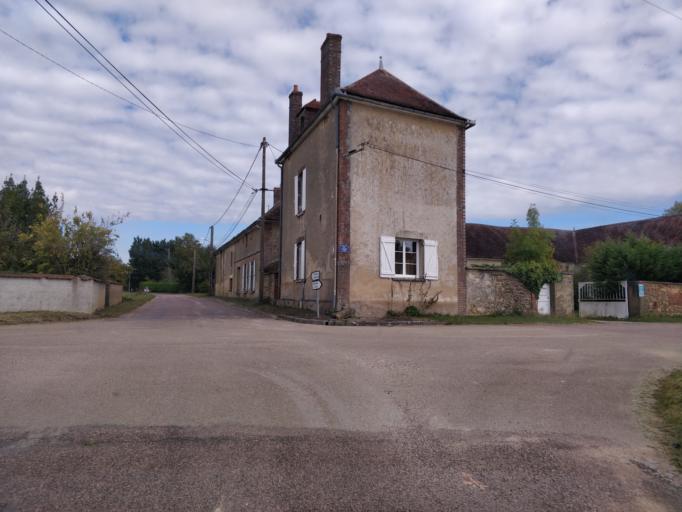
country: FR
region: Bourgogne
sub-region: Departement de l'Yonne
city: Vergigny
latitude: 47.9850
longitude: 3.6864
